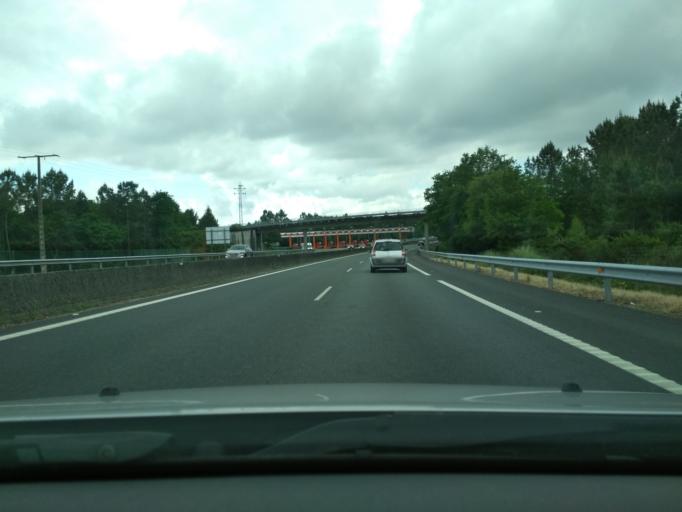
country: ES
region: Galicia
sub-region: Provincia da Coruna
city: Santiago de Compostela
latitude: 42.8201
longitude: -8.5707
